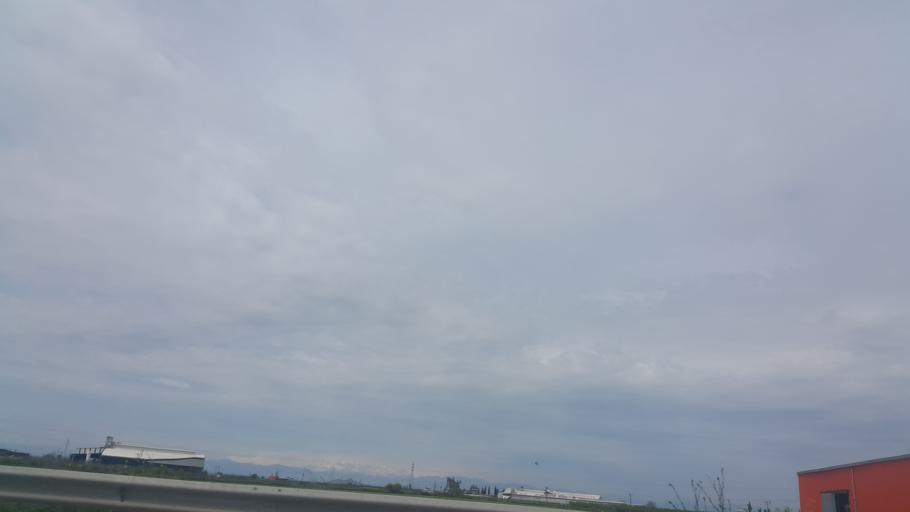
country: TR
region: Adana
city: Ceyhan
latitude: 37.0513
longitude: 35.7761
